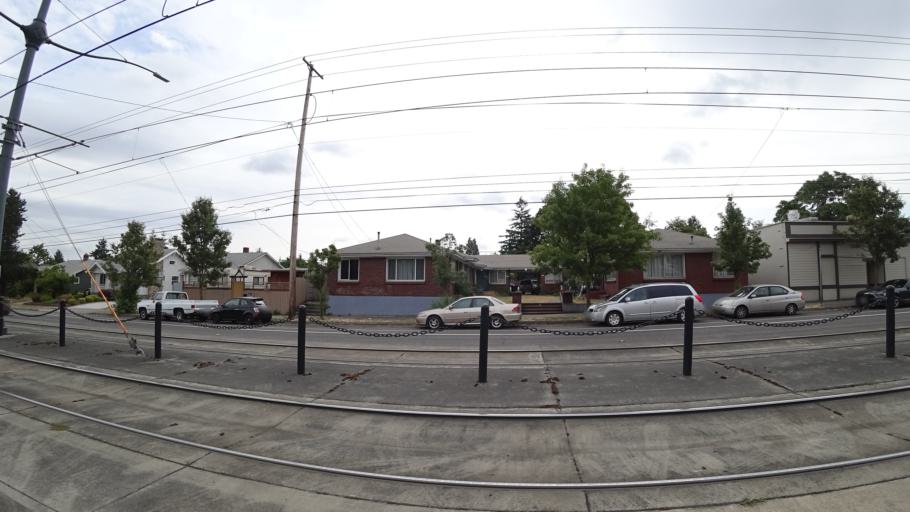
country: US
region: Oregon
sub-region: Multnomah County
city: Portland
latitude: 45.5731
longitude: -122.6822
